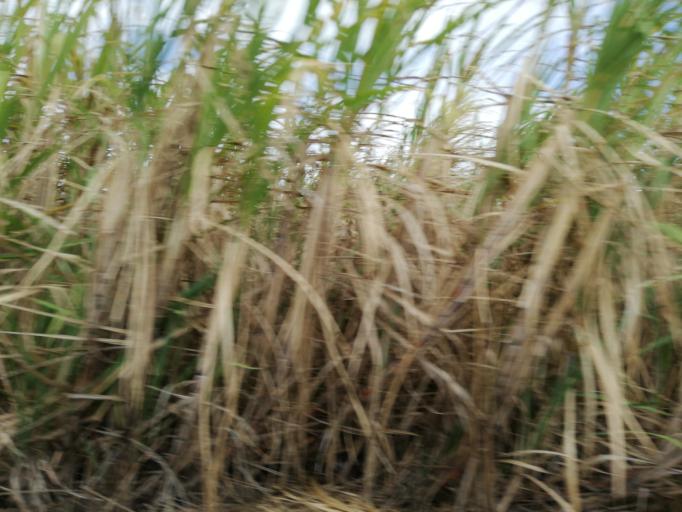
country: MU
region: Pamplemousses
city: Arsenal
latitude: -20.0941
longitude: 57.5452
